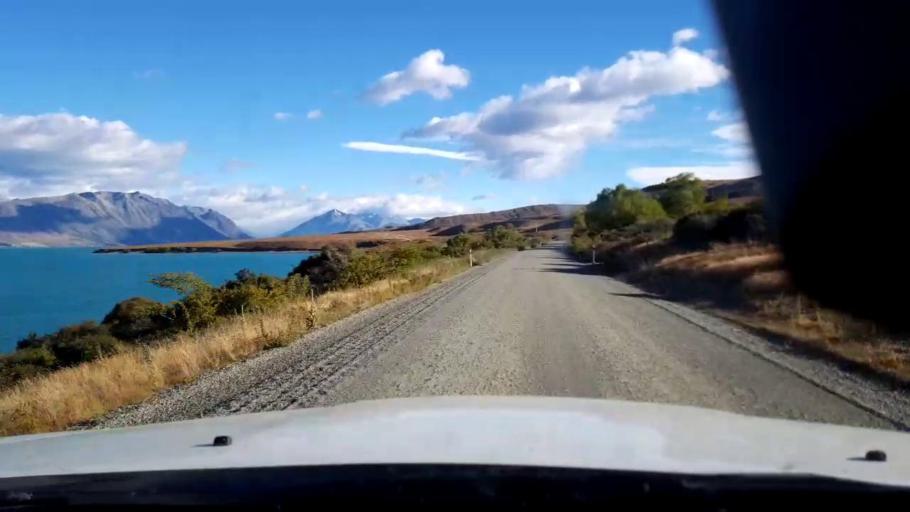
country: NZ
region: Canterbury
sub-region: Timaru District
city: Pleasant Point
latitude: -43.9319
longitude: 170.5591
